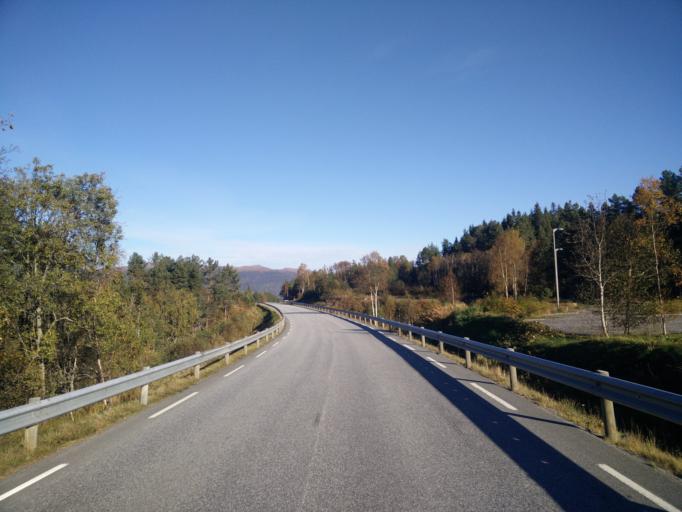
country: NO
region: More og Romsdal
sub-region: Halsa
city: Liaboen
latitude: 63.1271
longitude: 8.3735
